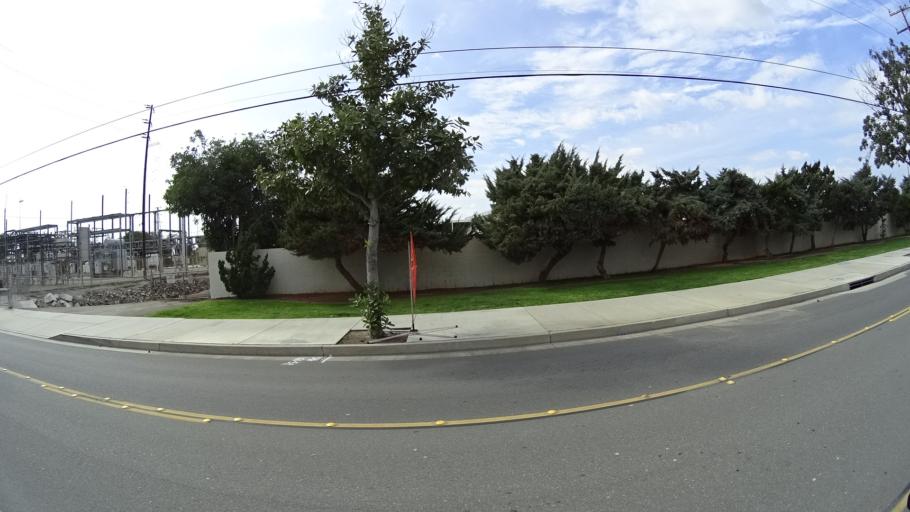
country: US
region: California
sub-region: Orange County
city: Buena Park
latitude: 33.8380
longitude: -117.9677
